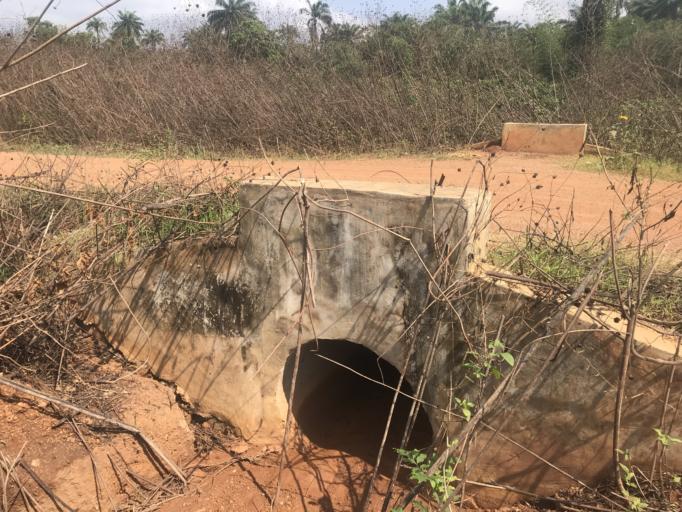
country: NG
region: Osun
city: Ikirun
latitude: 7.8475
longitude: 4.6327
